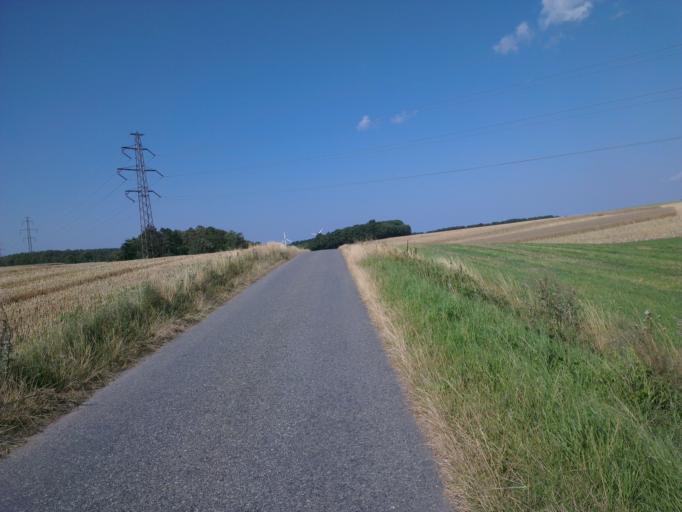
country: DK
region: Capital Region
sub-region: Frederikssund Kommune
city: Jaegerspris
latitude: 55.8078
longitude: 11.9021
